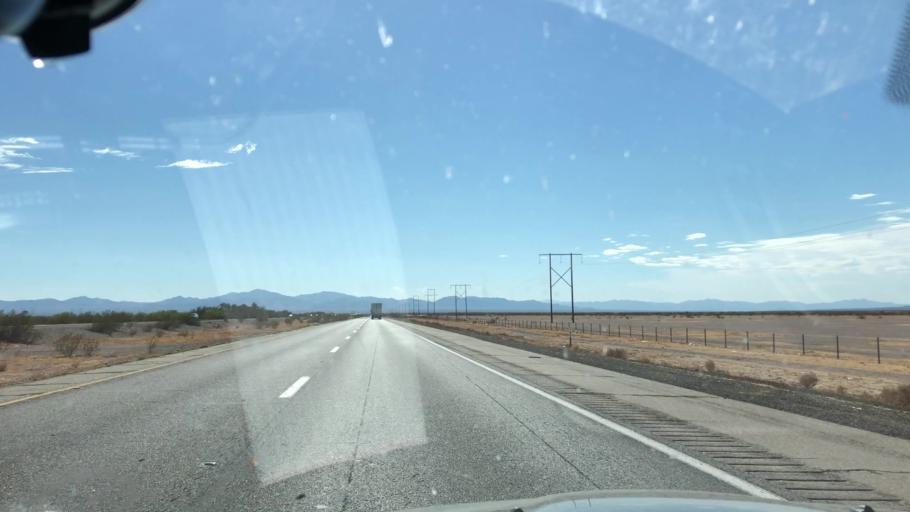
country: US
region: California
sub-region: Riverside County
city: Mesa Verde
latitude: 33.6063
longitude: -114.9365
